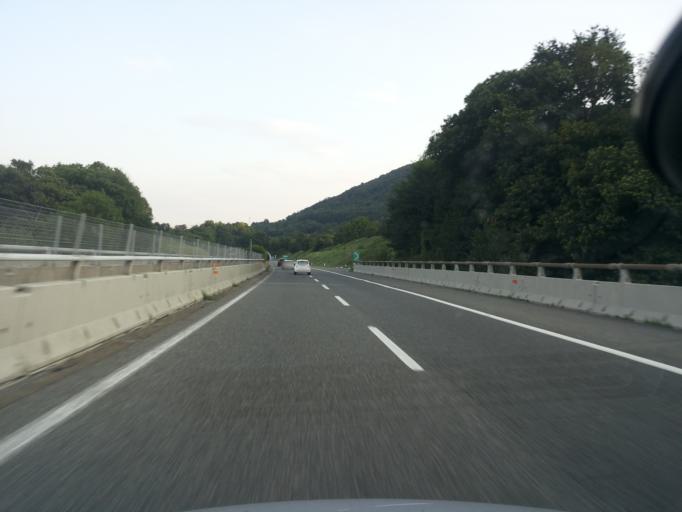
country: IT
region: Piedmont
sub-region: Provincia Verbano-Cusio-Ossola
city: Brovello
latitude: 45.8450
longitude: 8.5344
